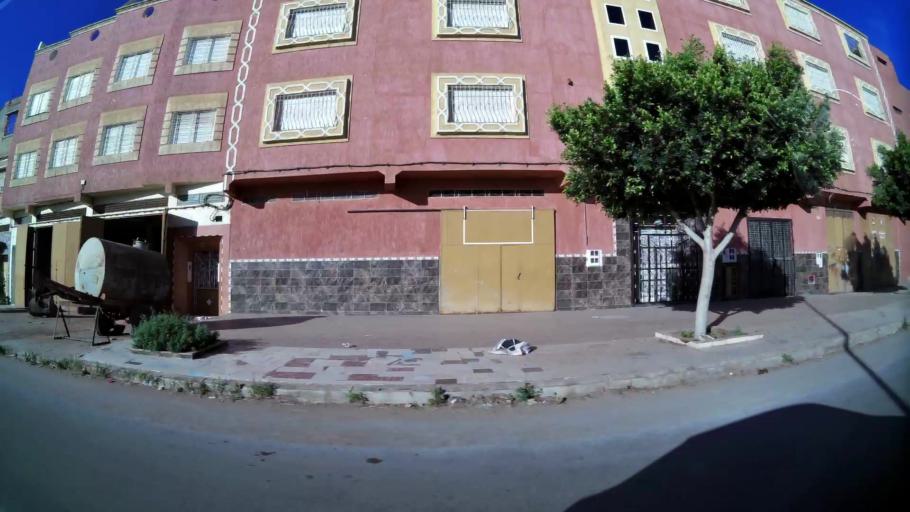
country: MA
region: Oriental
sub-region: Berkane-Taourirt
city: Berkane
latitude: 34.9243
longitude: -2.3403
